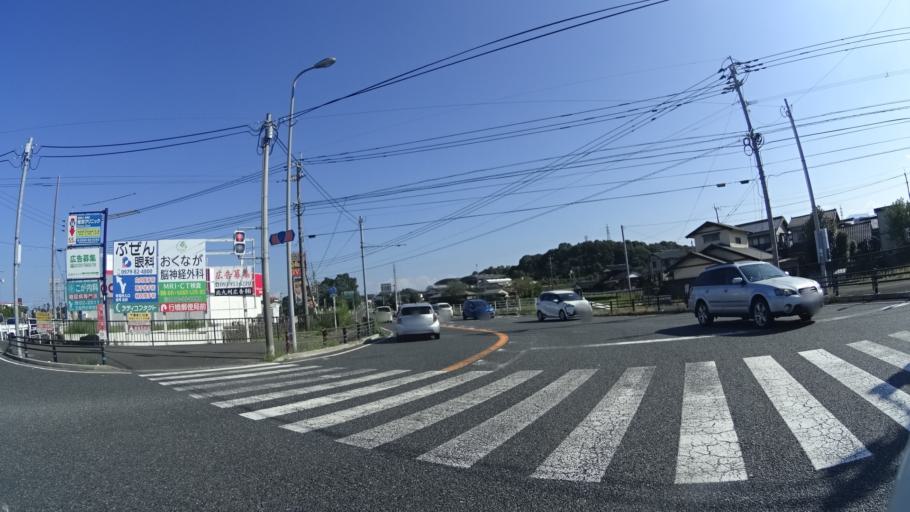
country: JP
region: Fukuoka
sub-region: Buzen-shi
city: Buzen
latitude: 33.6164
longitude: 131.0995
